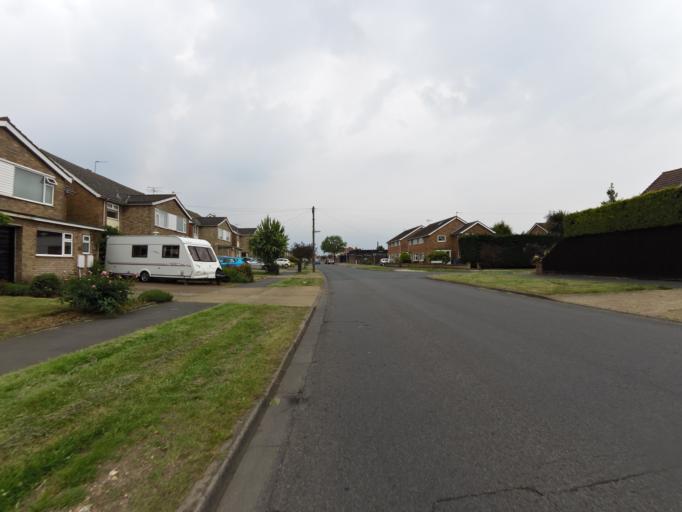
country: GB
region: England
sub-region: Suffolk
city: Ipswich
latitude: 52.0839
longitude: 1.1460
